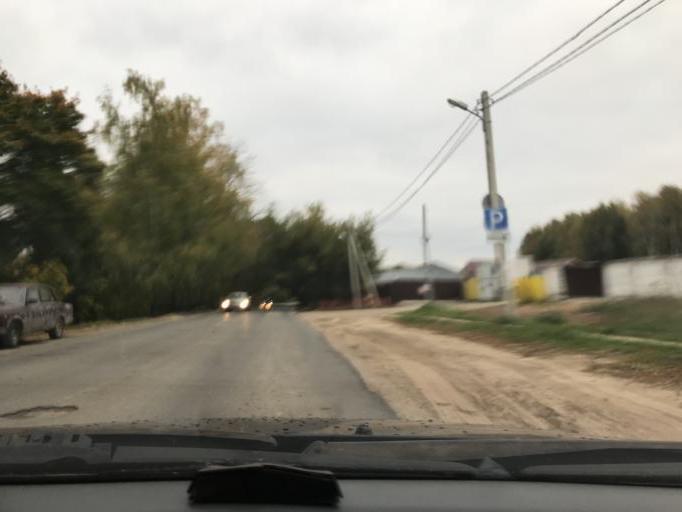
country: RU
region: Kaluga
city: Kaluga
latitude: 54.5691
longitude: 36.2216
